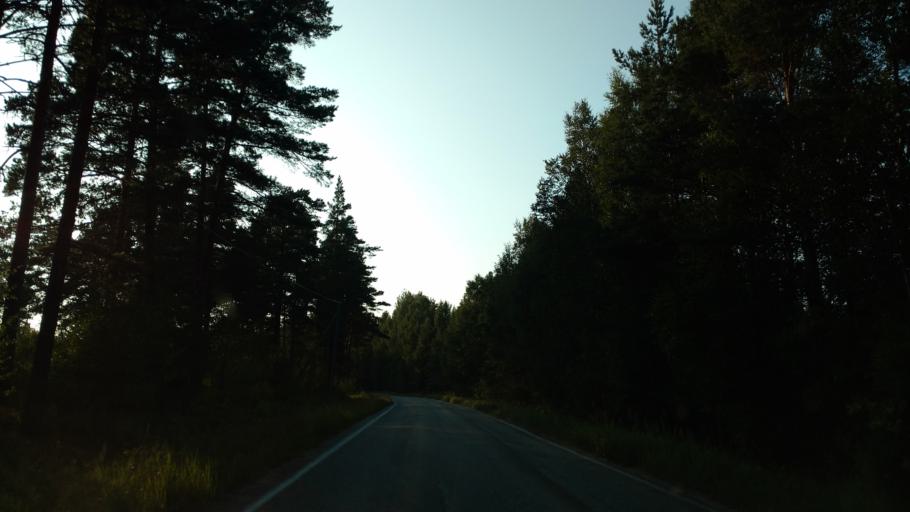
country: FI
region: Varsinais-Suomi
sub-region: Salo
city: Saerkisalo
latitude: 60.1876
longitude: 22.9581
